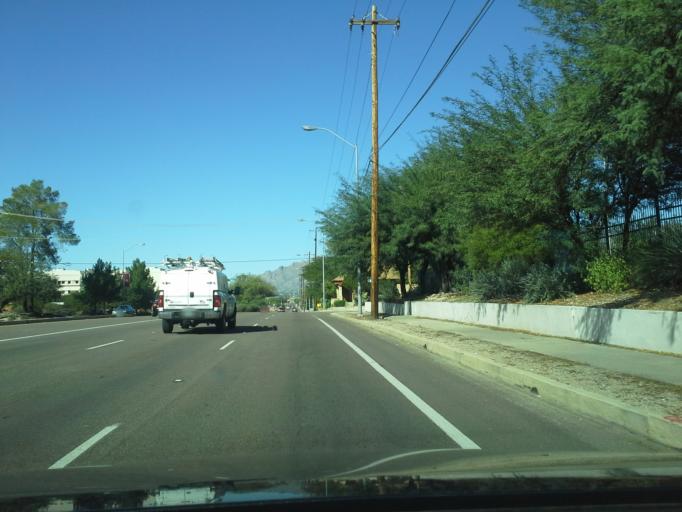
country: US
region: Arizona
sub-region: Pima County
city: Tucson
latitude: 32.2380
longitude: -110.9439
